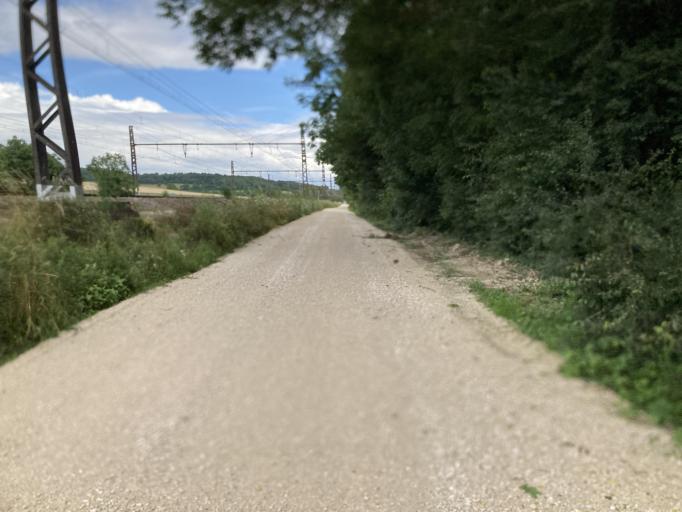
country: FR
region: Bourgogne
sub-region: Departement de la Cote-d'Or
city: Montbard
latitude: 47.6162
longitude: 4.3771
